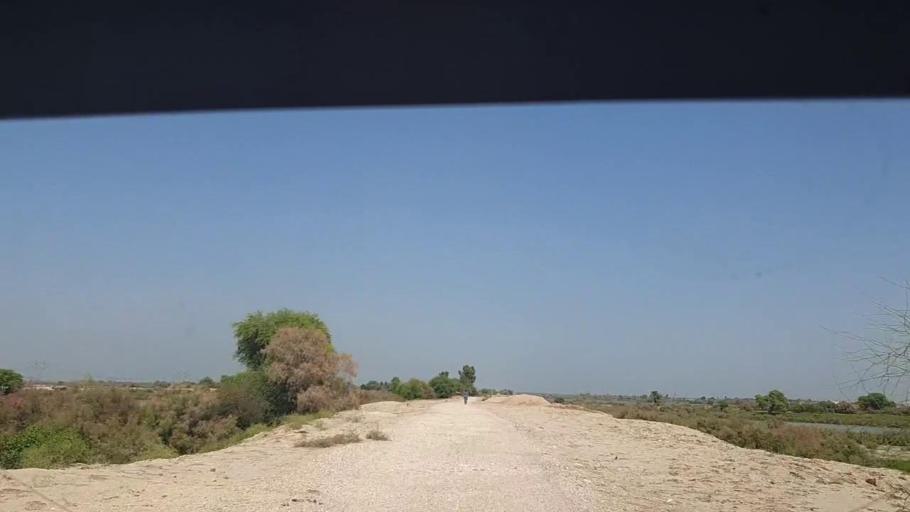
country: PK
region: Sindh
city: Kandhkot
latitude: 28.1926
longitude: 69.1663
